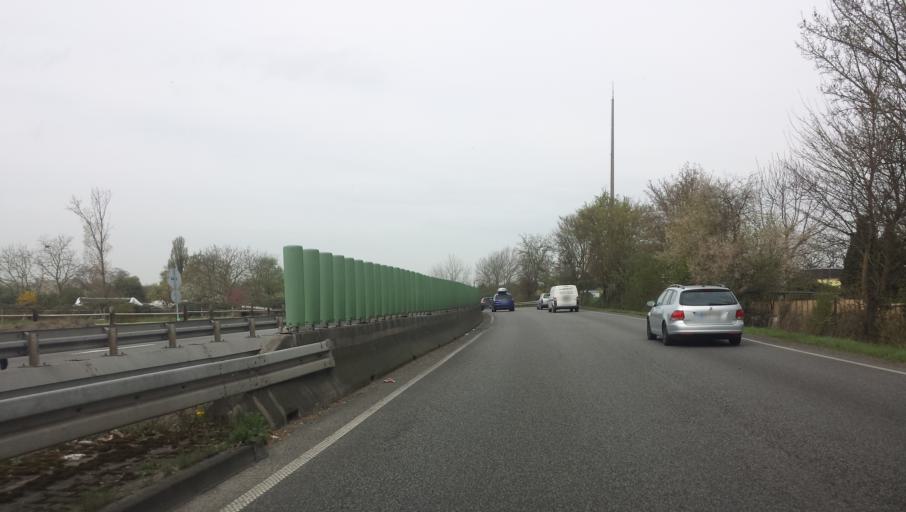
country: DE
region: Hesse
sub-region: Regierungsbezirk Darmstadt
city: Maintal
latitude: 50.1356
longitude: 8.8251
